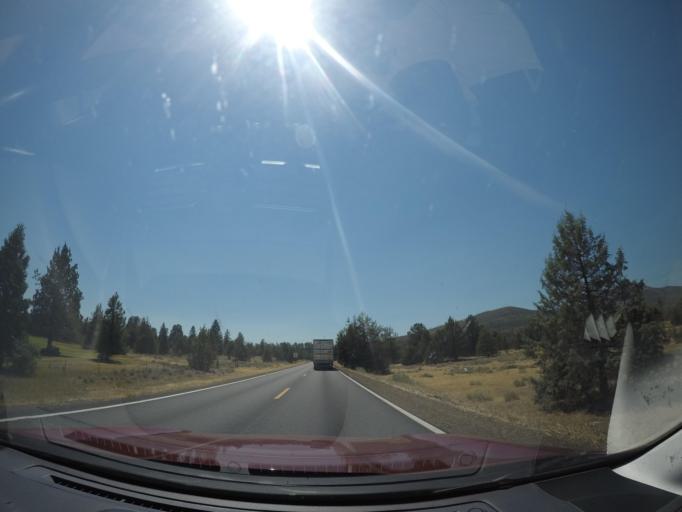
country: US
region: California
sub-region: Shasta County
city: Burney
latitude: 40.9996
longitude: -121.4513
